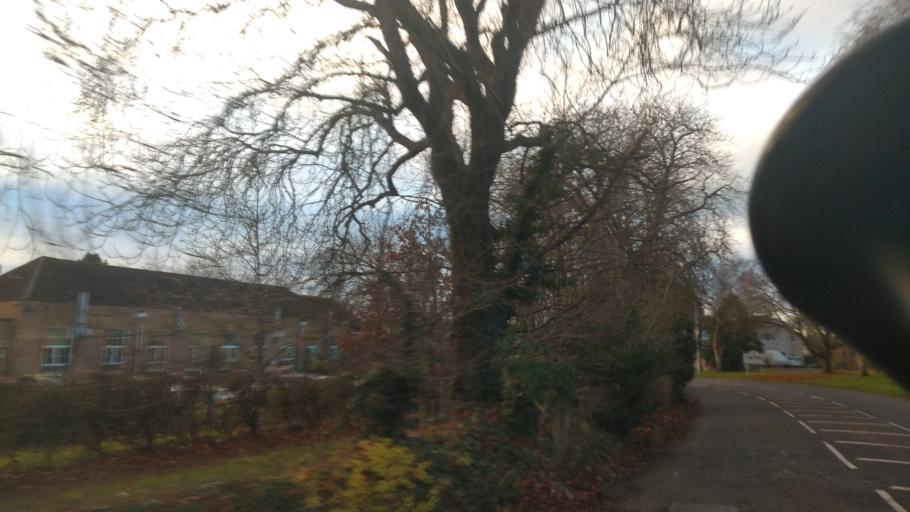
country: GB
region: England
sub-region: Somerset
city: Frome
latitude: 51.2437
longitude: -2.3122
